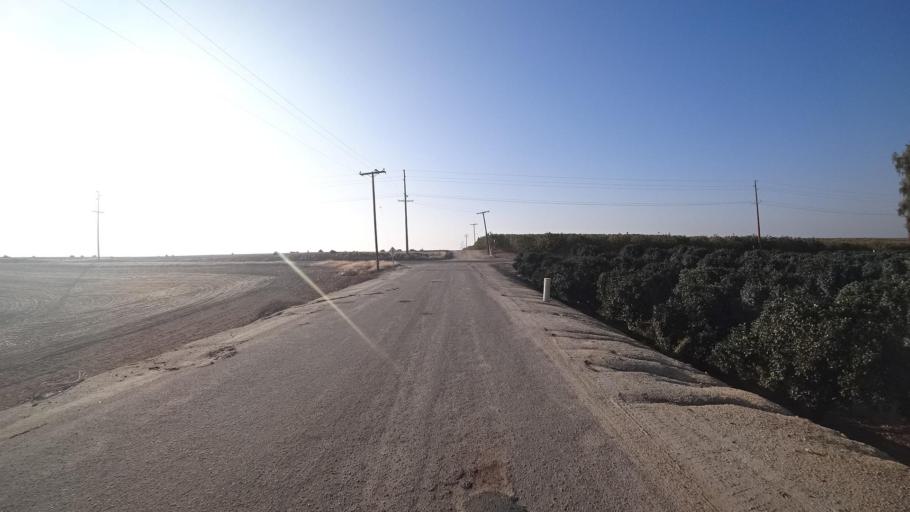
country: US
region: California
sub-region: Tulare County
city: Richgrove
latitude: 35.7626
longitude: -119.0807
